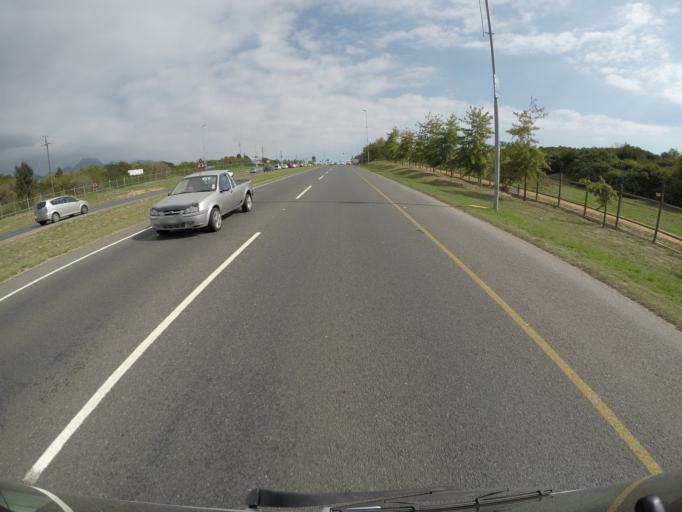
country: ZA
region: Western Cape
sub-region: Cape Winelands District Municipality
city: Stellenbosch
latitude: -33.9732
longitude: 18.8425
